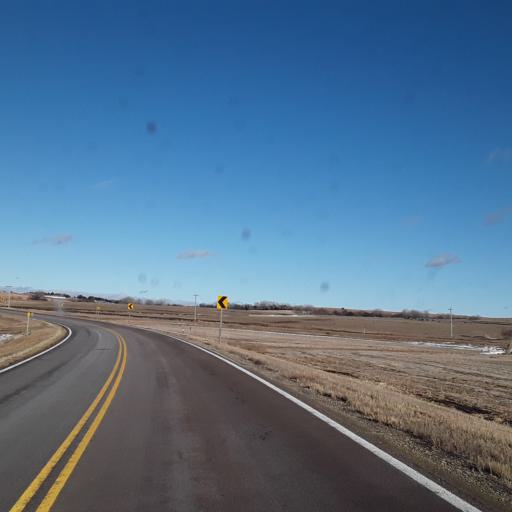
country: US
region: Kansas
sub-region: Cloud County
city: Concordia
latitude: 39.4969
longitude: -97.7250
